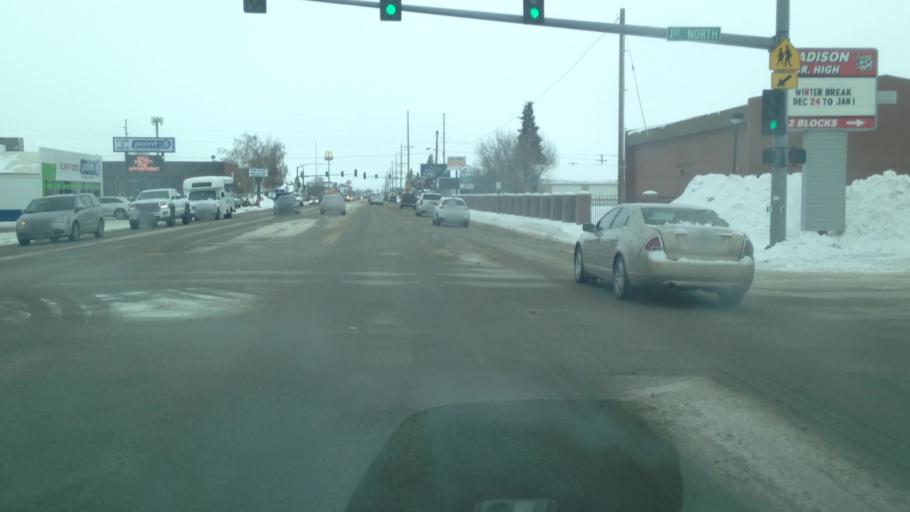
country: US
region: Idaho
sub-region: Madison County
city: Rexburg
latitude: 43.8282
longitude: -111.7781
